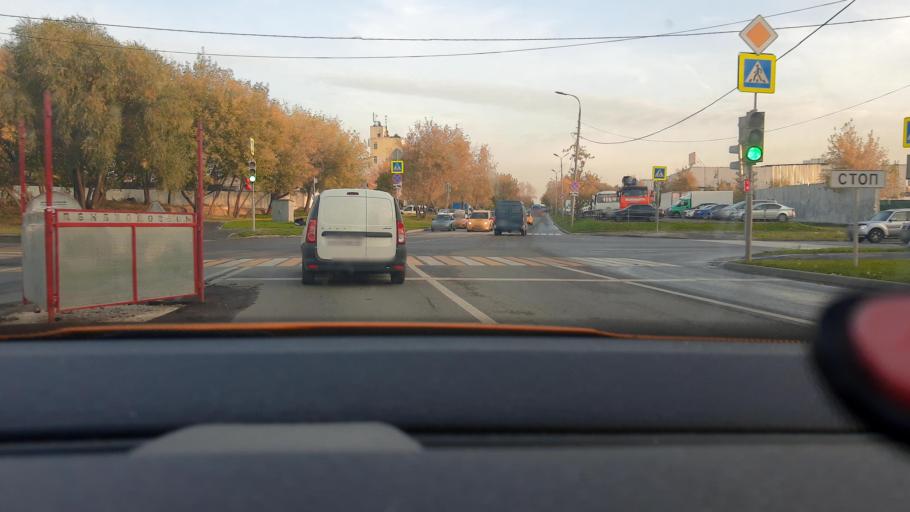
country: RU
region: Moscow
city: Metrogorodok
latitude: 55.8172
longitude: 37.7693
